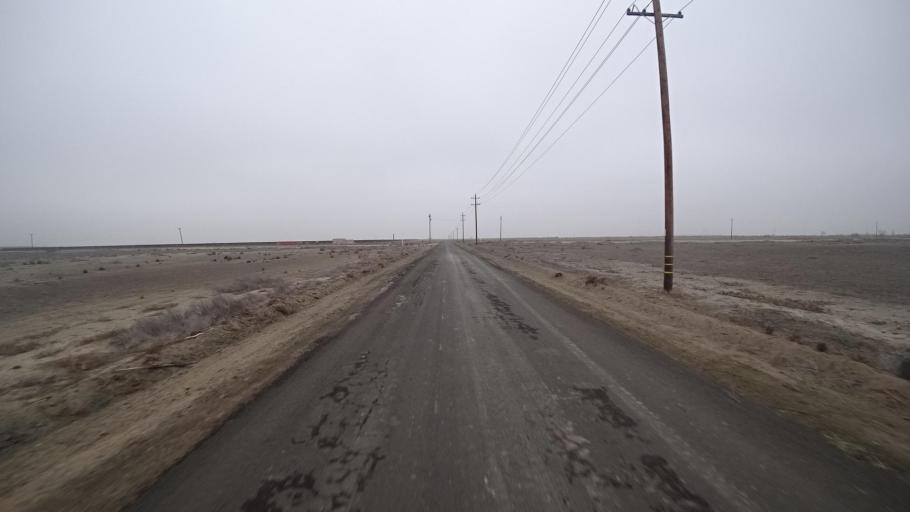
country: US
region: California
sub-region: Kern County
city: Lost Hills
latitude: 35.5951
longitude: -119.5805
